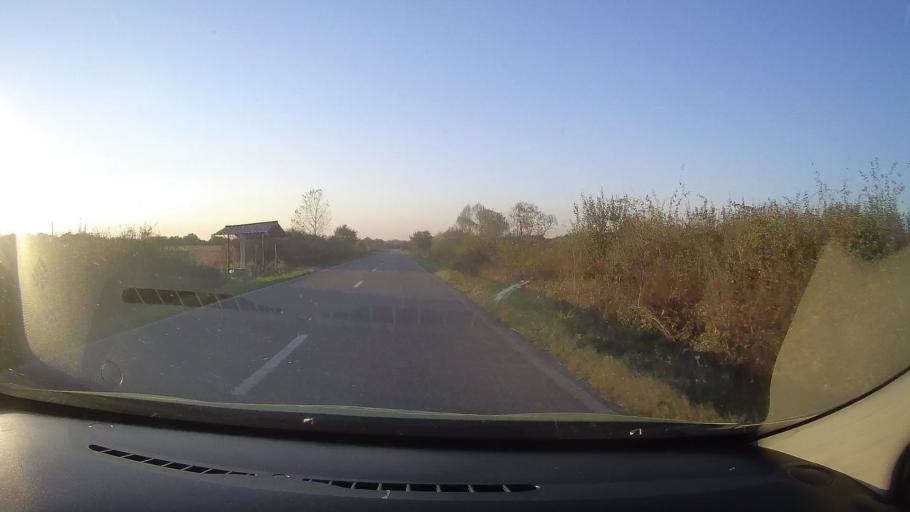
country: RO
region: Timis
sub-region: Comuna Traian Vuia
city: Traian Vuia
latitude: 45.7889
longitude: 22.0769
